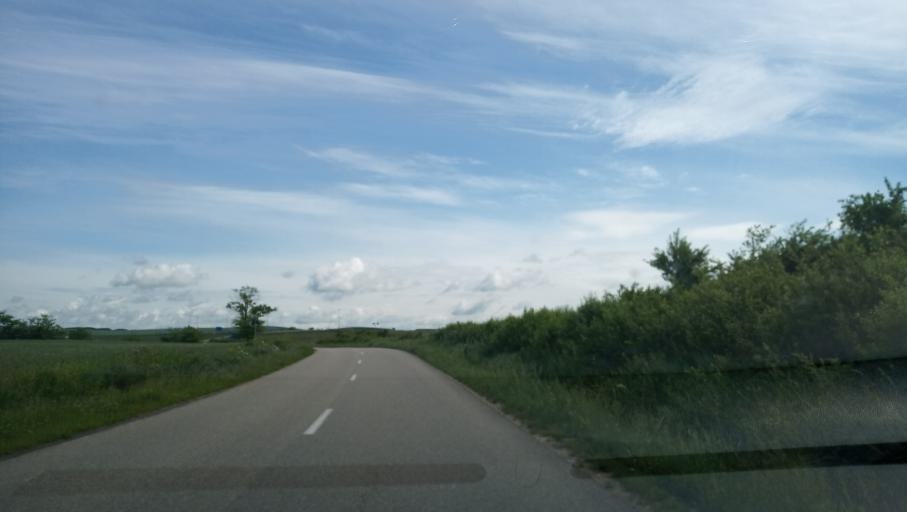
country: RO
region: Timis
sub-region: Comuna Topolovatu Mare
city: Topolovatu Mare
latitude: 45.7911
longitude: 21.6533
